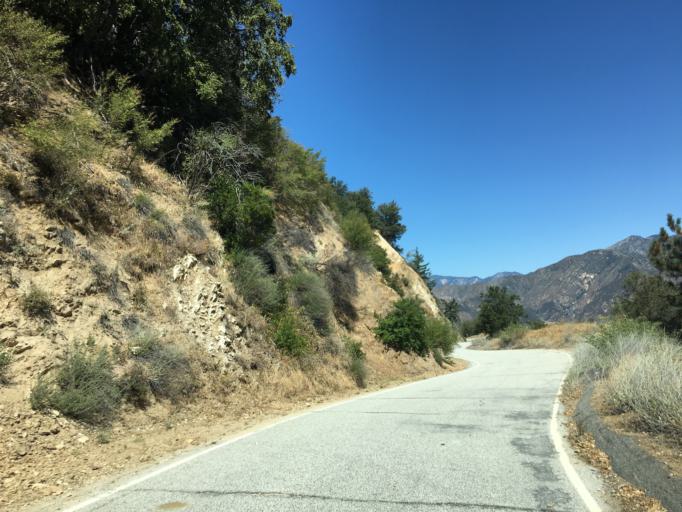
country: US
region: California
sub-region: San Bernardino County
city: San Antonio Heights
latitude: 34.2230
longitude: -117.7258
